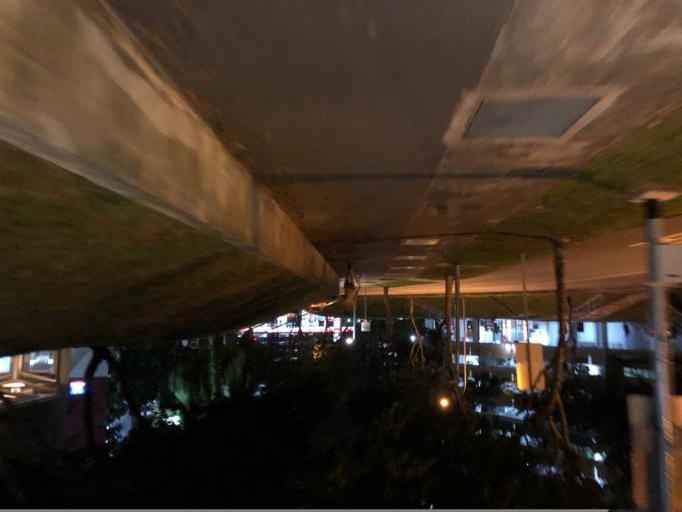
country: MY
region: Johor
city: Kampung Pasir Gudang Baru
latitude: 1.4318
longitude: 103.8385
